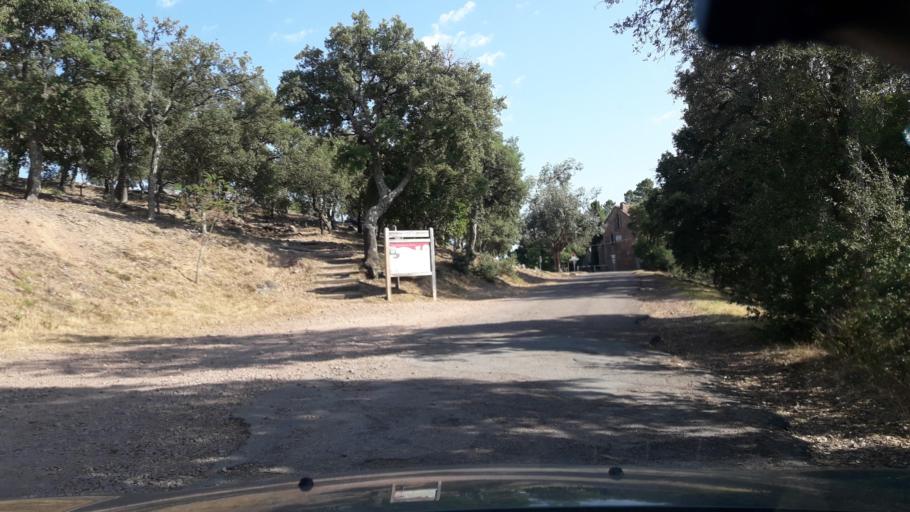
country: FR
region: Provence-Alpes-Cote d'Azur
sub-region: Departement du Var
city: Saint-Raphael
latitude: 43.4965
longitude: 6.8016
